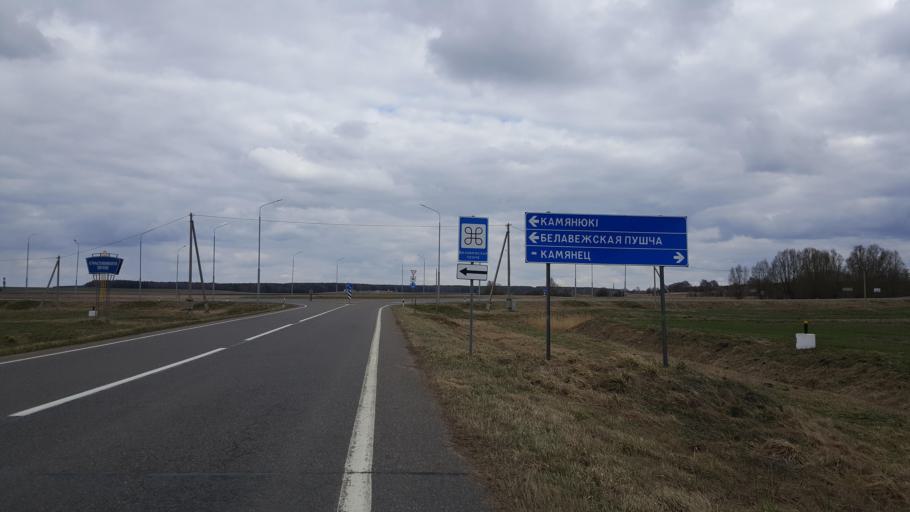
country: BY
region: Brest
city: Kamyanyuki
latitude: 52.4955
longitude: 23.7801
